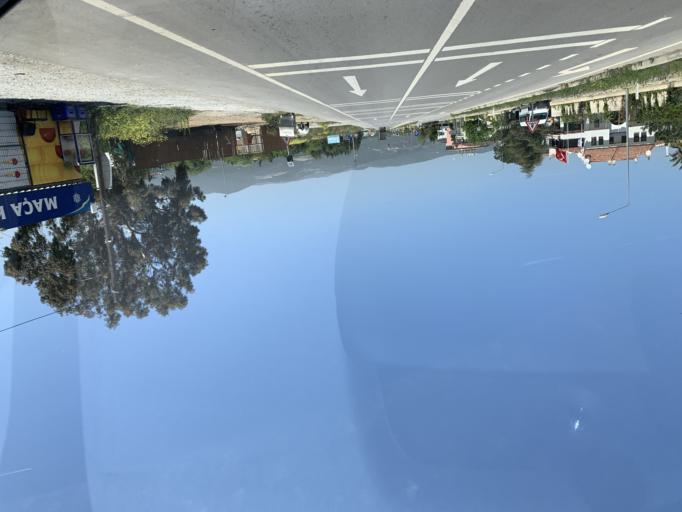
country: TR
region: Bursa
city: Iznik
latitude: 40.4096
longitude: 29.7067
